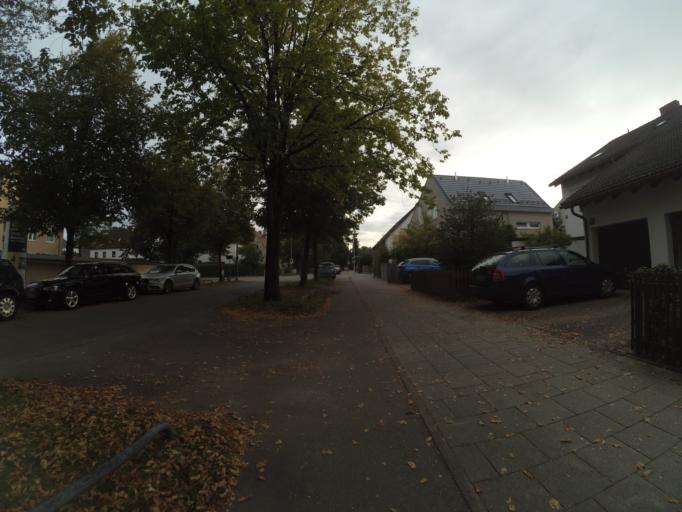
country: DE
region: Bavaria
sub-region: Upper Bavaria
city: Karlsfeld
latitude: 48.1760
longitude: 11.5127
